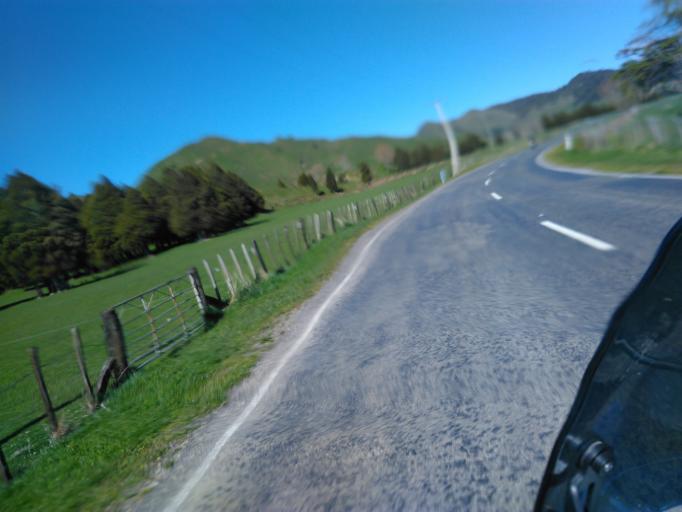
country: NZ
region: Bay of Plenty
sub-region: Opotiki District
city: Opotiki
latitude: -38.2912
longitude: 177.5304
